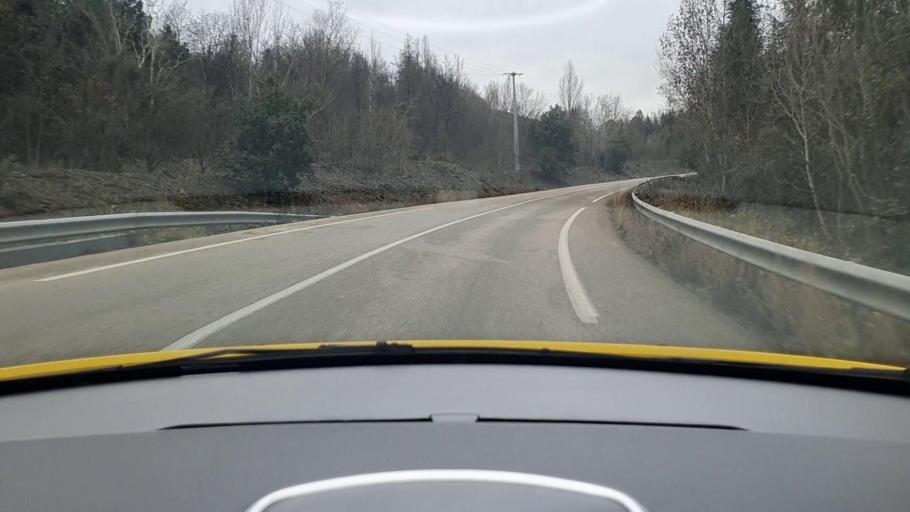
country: FR
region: Languedoc-Roussillon
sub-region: Departement du Gard
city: Laval-Pradel
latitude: 44.2219
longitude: 4.0843
